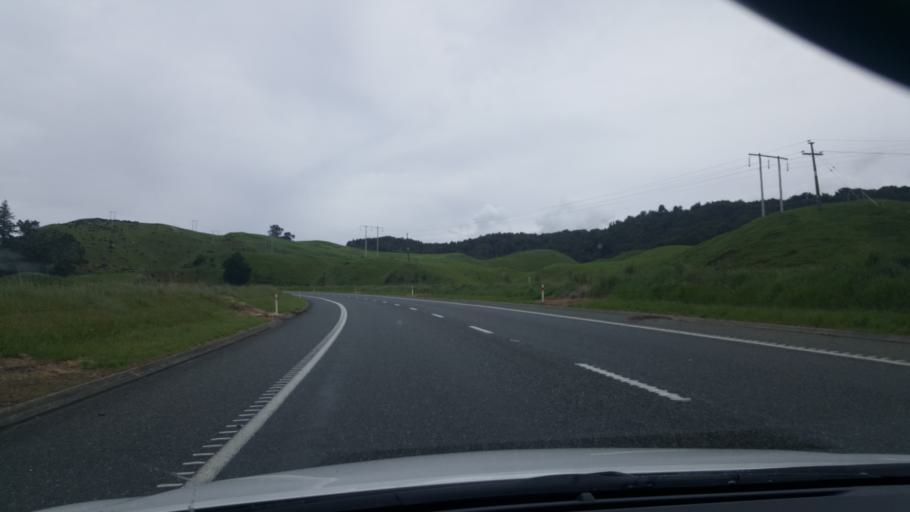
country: NZ
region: Bay of Plenty
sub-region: Rotorua District
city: Rotorua
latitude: -38.2612
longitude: 176.3202
